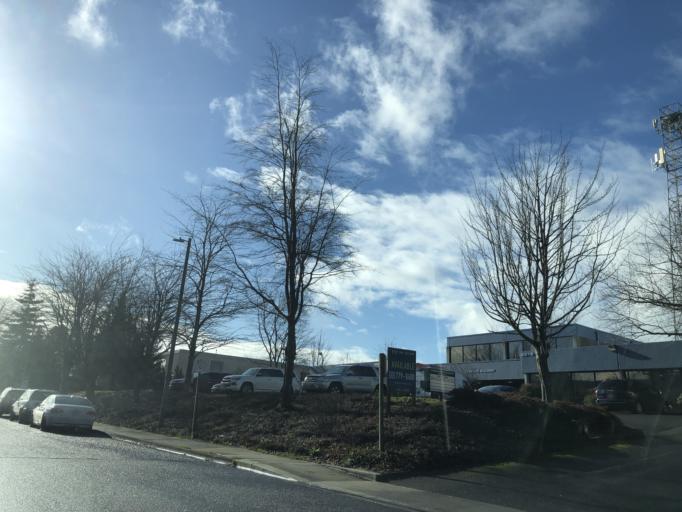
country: US
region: Washington
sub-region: Pierce County
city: Tacoma
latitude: 47.2392
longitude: -122.4651
